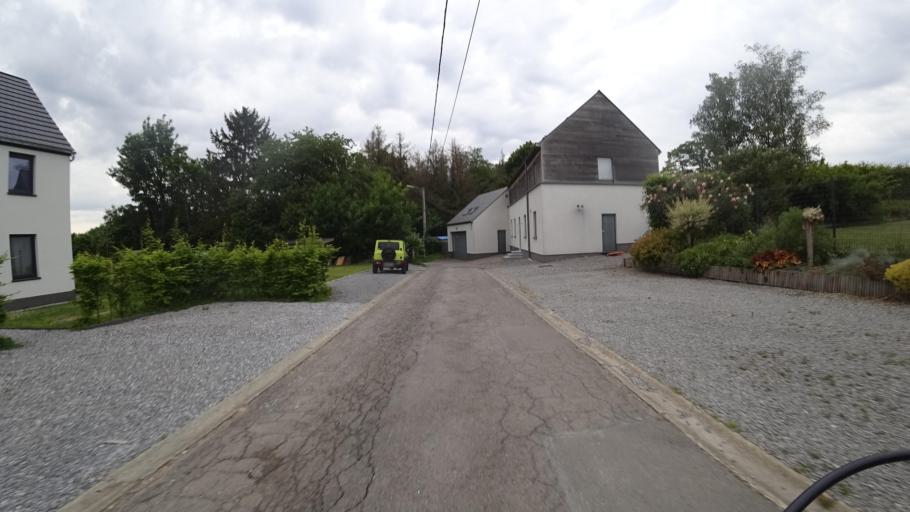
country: BE
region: Wallonia
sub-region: Province du Brabant Wallon
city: Perwez
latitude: 50.5699
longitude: 4.7707
